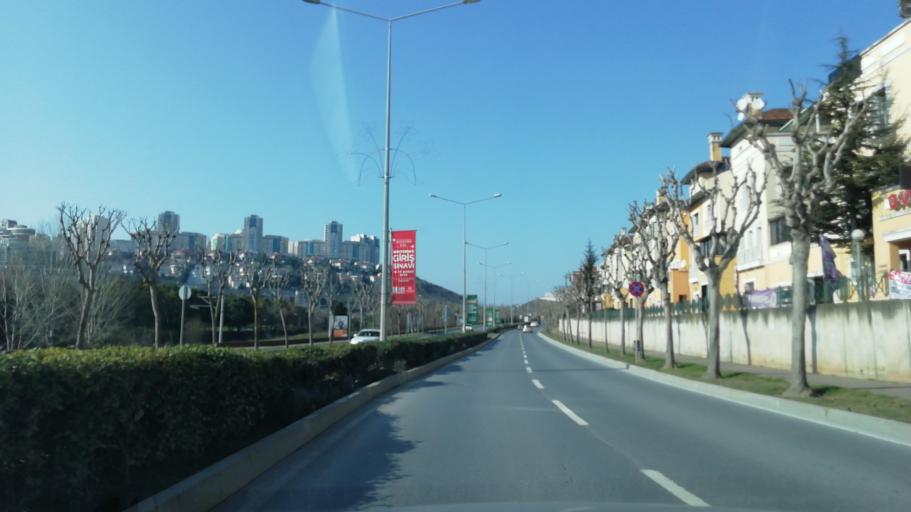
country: TR
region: Istanbul
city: Esenyurt
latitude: 41.0685
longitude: 28.6950
